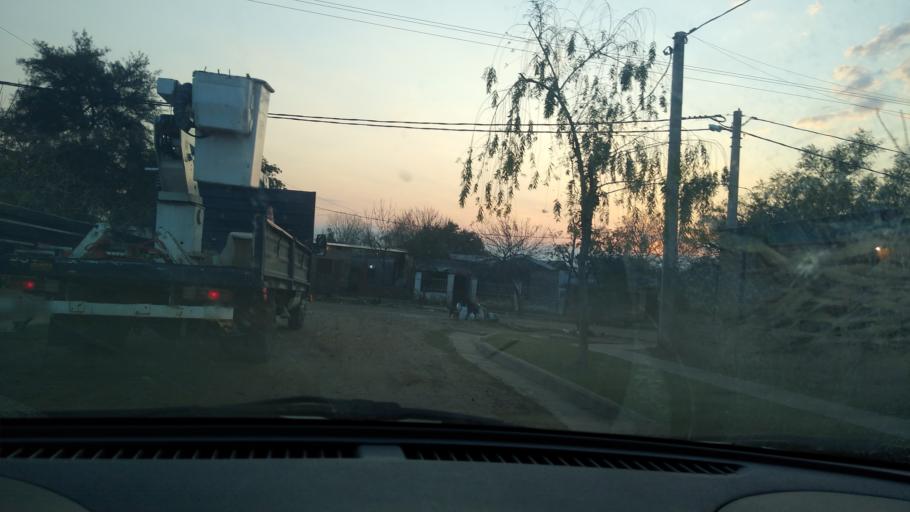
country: AR
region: Chaco
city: Resistencia
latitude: -27.4594
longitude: -58.9633
